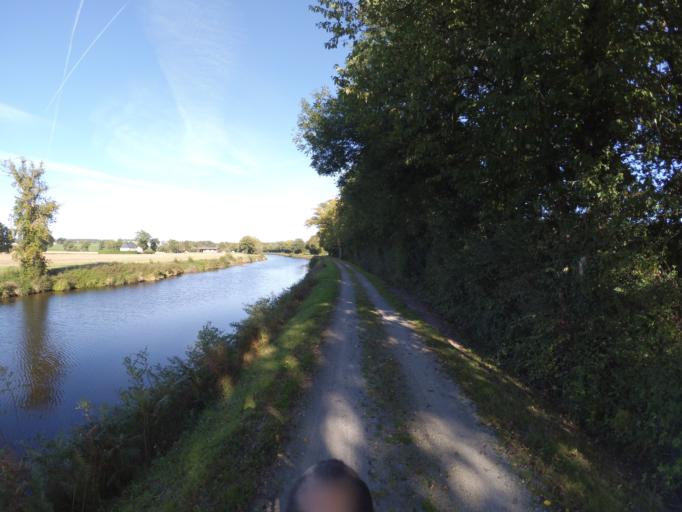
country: FR
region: Brittany
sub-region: Departement du Morbihan
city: Saint-Martin-sur-Oust
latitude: 47.7368
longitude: -2.2475
